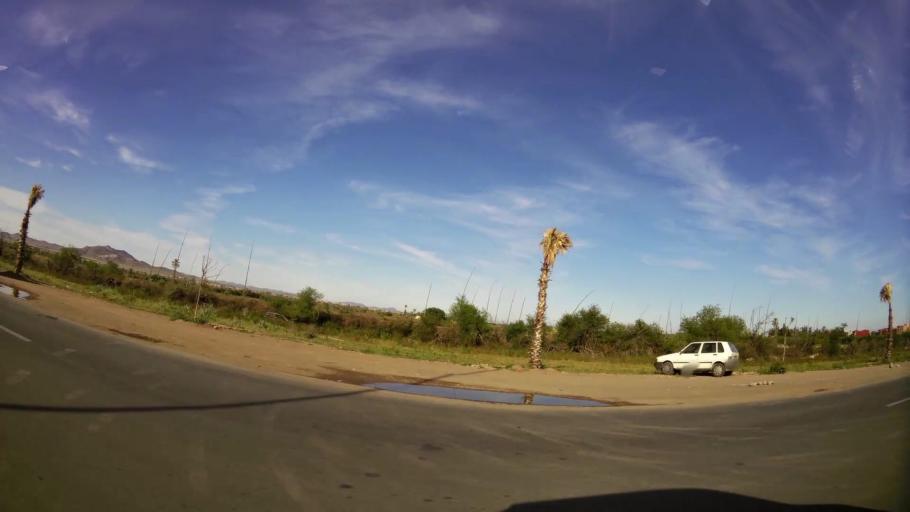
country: MA
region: Marrakech-Tensift-Al Haouz
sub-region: Marrakech
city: Marrakesh
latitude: 31.6843
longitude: -8.0512
